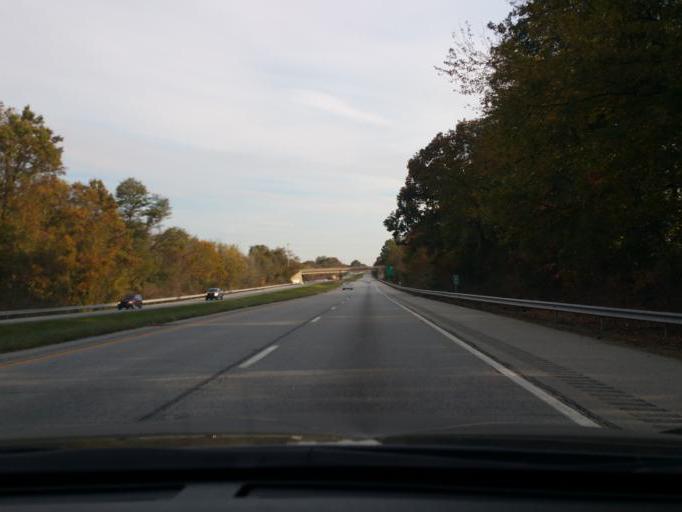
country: US
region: Pennsylvania
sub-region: Chester County
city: Oxford
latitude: 39.7761
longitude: -76.0061
